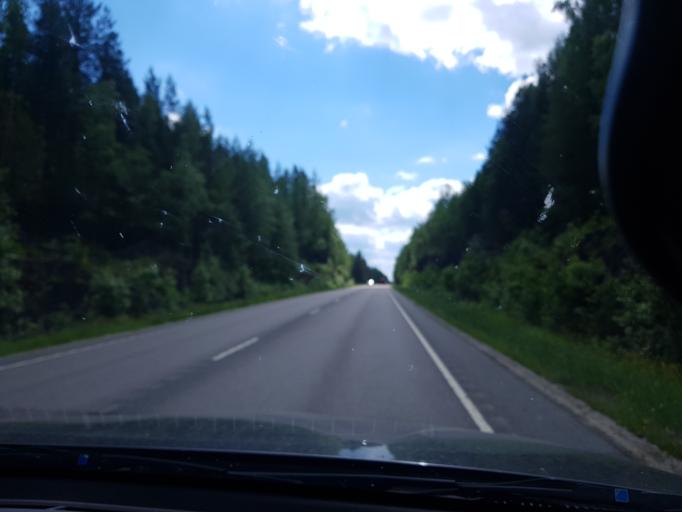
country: FI
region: Haeme
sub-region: Haemeenlinna
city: Parola
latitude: 61.0879
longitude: 24.4000
